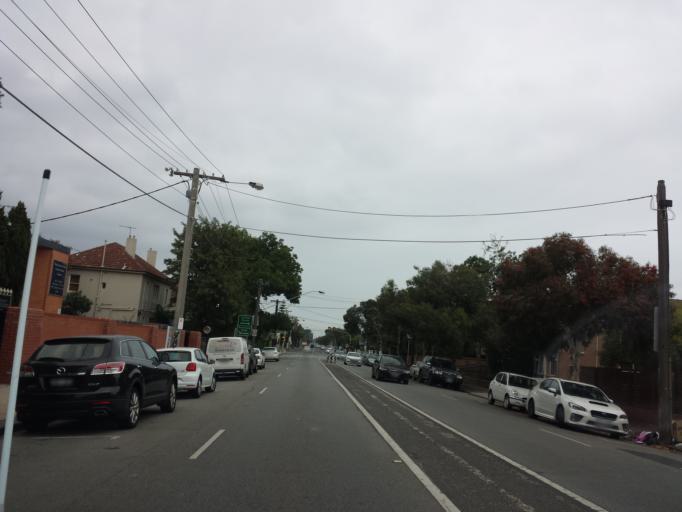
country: AU
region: Victoria
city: Balaclava
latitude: -37.8682
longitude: 144.9997
